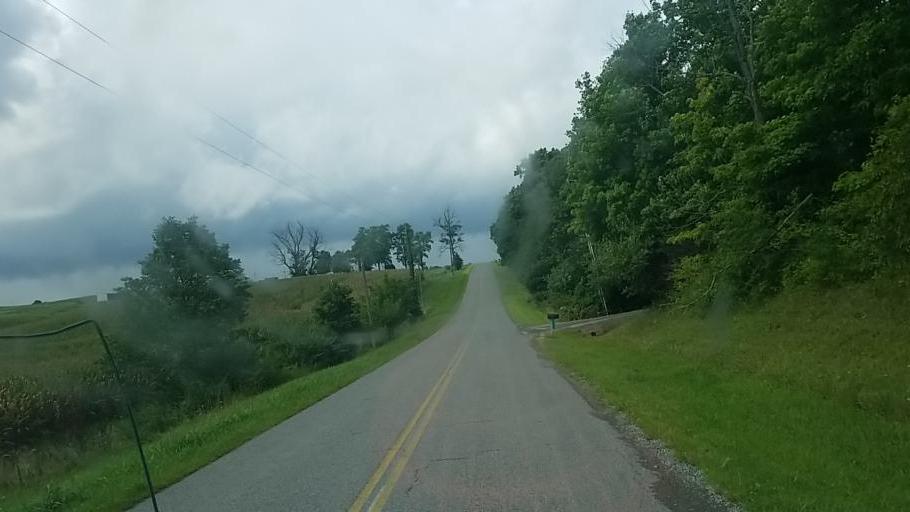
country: US
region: Ohio
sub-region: Champaign County
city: North Lewisburg
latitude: 40.2470
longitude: -83.6494
